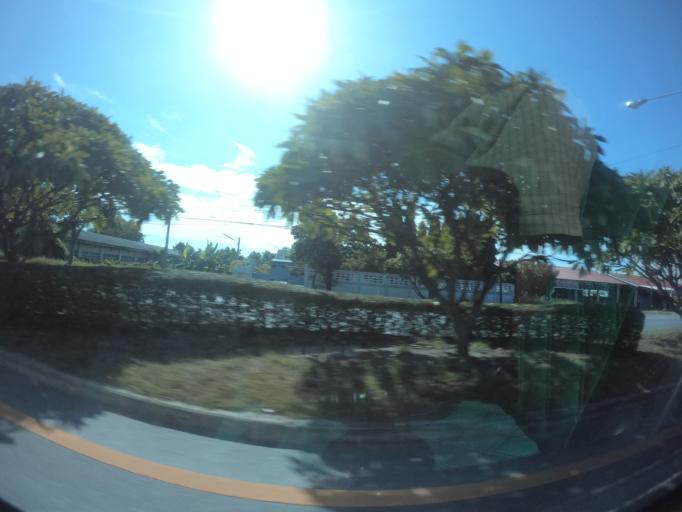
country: TH
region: Nakhon Nayok
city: Ban Na
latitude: 14.2560
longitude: 101.0727
